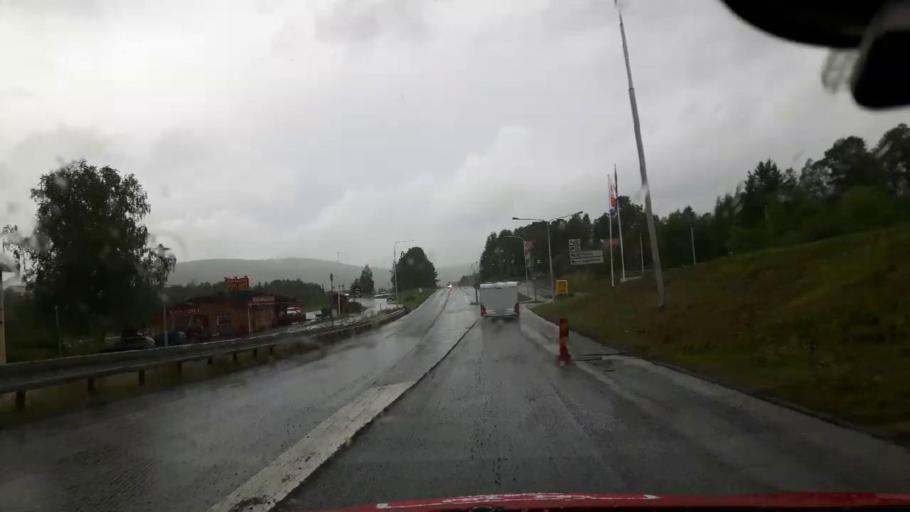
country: SE
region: Jaemtland
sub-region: Are Kommun
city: Jarpen
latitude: 63.3426
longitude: 13.4731
